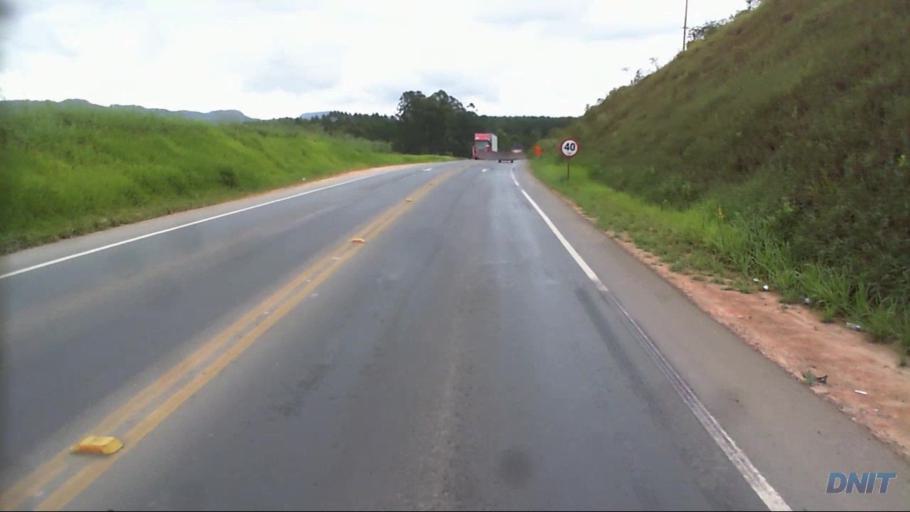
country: BR
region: Minas Gerais
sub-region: Barao De Cocais
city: Barao de Cocais
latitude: -19.7549
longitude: -43.4733
